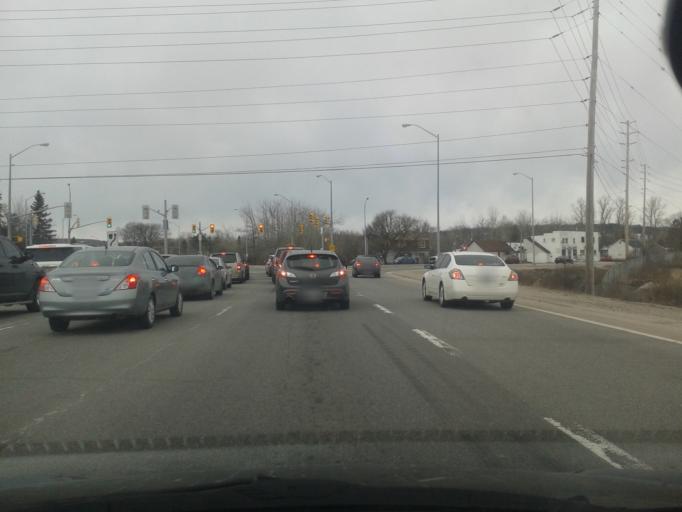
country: CA
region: Ontario
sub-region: Nipissing District
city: North Bay
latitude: 46.3177
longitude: -79.4433
